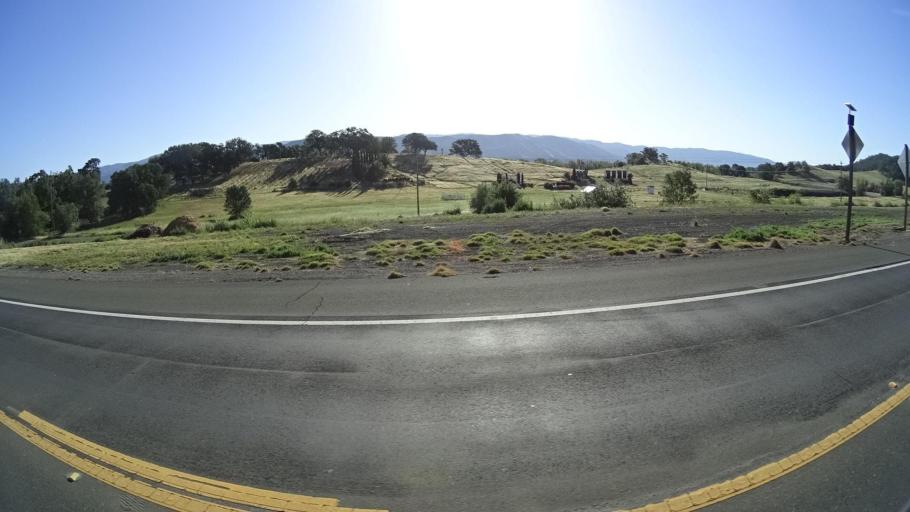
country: US
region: California
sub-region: Lake County
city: Upper Lake
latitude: 39.1302
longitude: -122.9081
